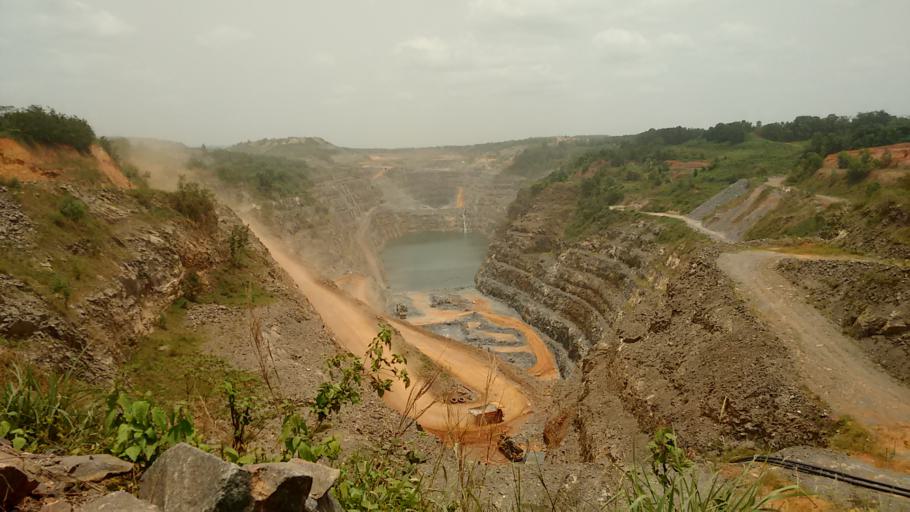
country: GH
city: Aboso
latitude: 5.5053
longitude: -1.8474
